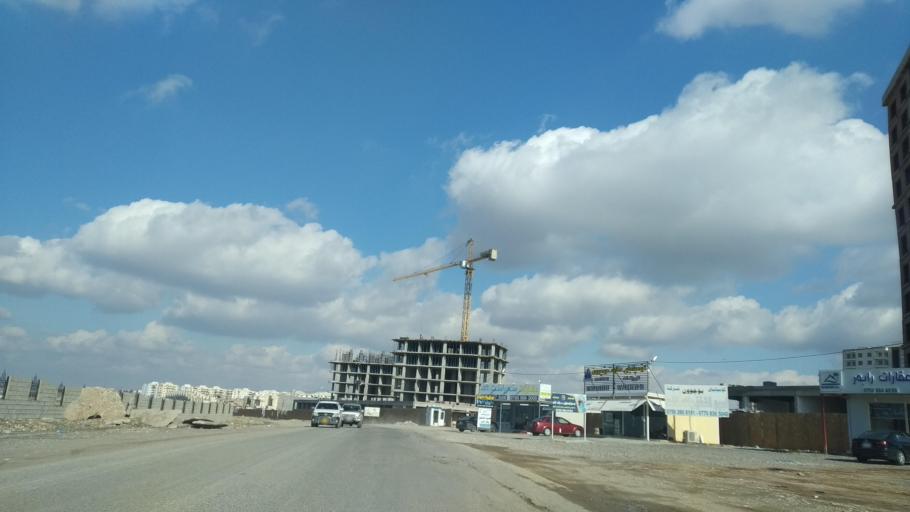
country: IQ
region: Arbil
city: Erbil
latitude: 36.2139
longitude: 44.1374
